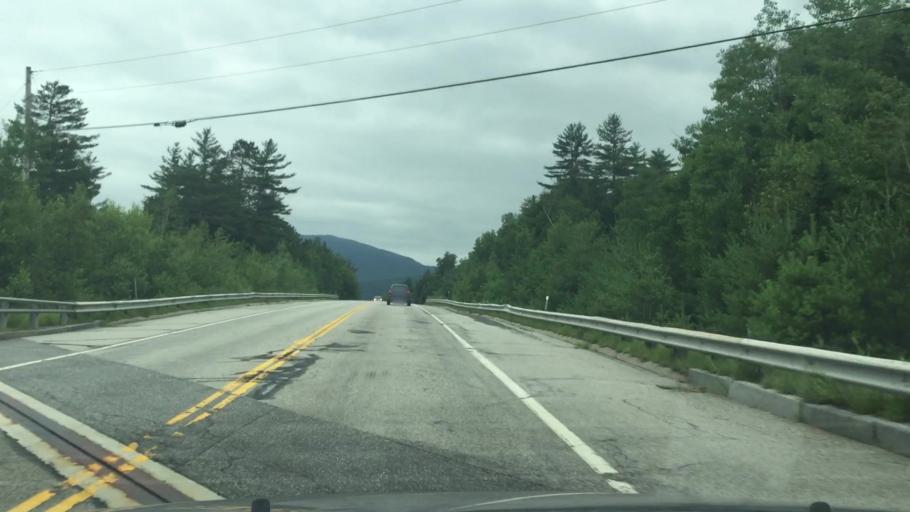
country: US
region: New Hampshire
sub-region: Carroll County
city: North Conway
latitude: 44.1132
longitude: -71.3539
